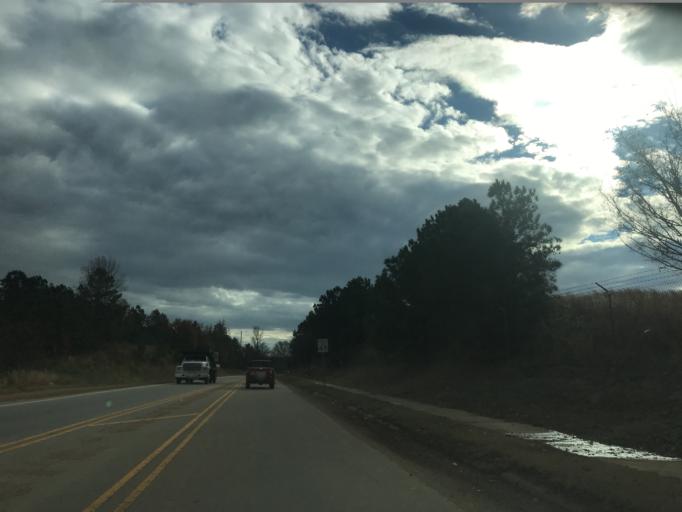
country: US
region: North Carolina
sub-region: Wake County
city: Raleigh
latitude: 35.7867
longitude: -78.5606
